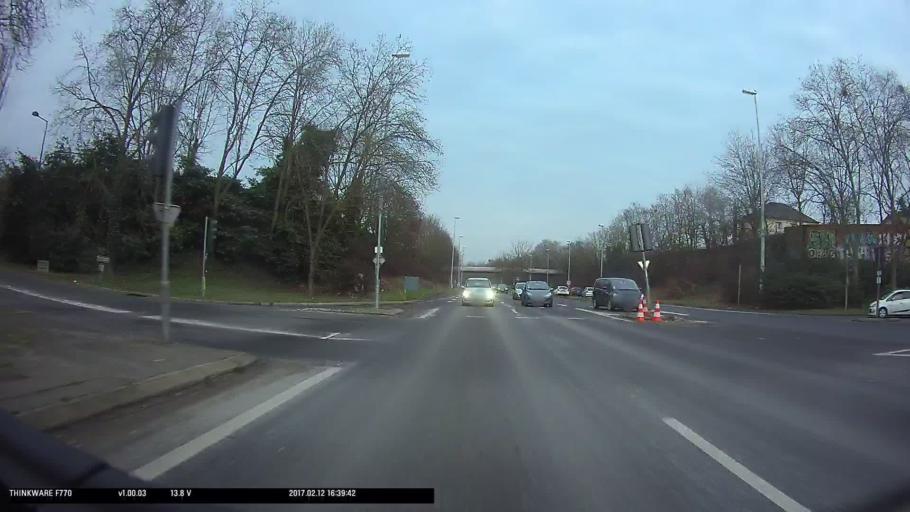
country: FR
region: Ile-de-France
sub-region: Departement du Val-d'Oise
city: Eragny
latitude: 49.0209
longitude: 2.1001
